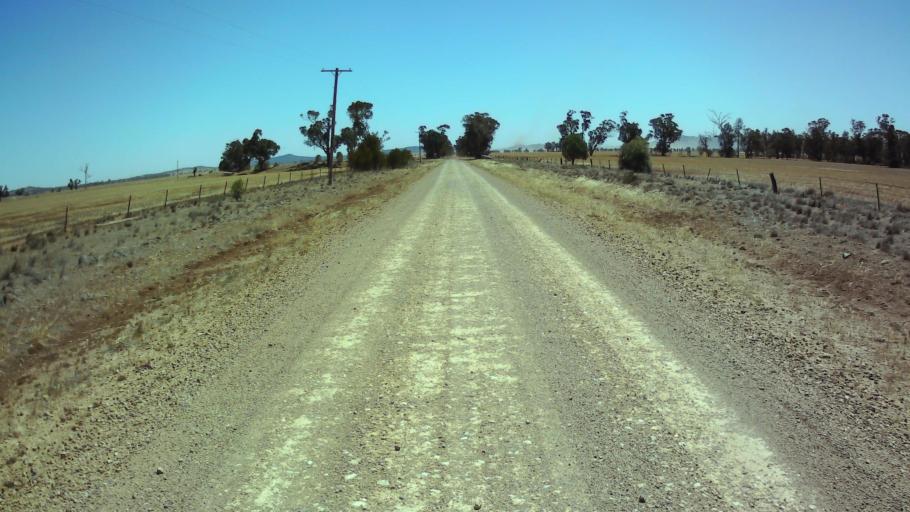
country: AU
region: New South Wales
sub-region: Forbes
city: Forbes
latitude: -33.6820
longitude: 147.7102
